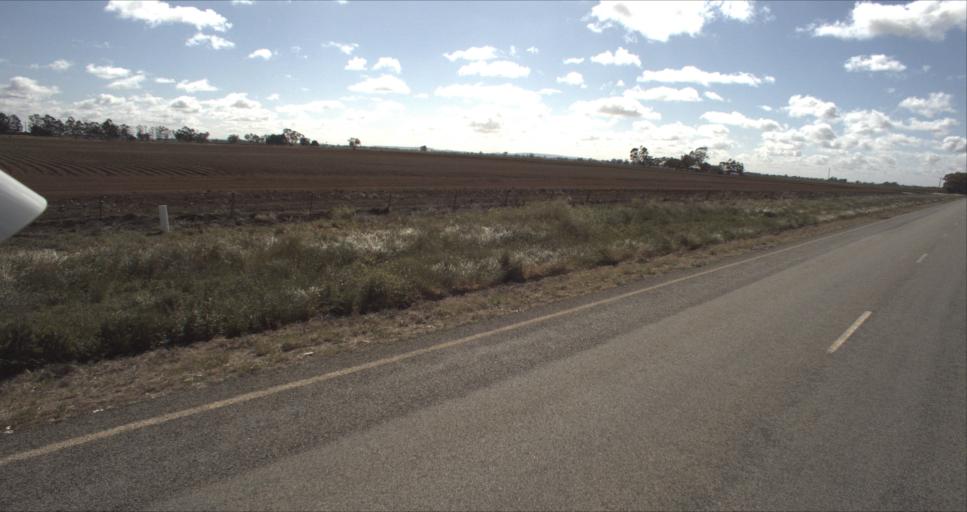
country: AU
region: New South Wales
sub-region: Leeton
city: Leeton
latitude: -34.5420
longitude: 146.2486
